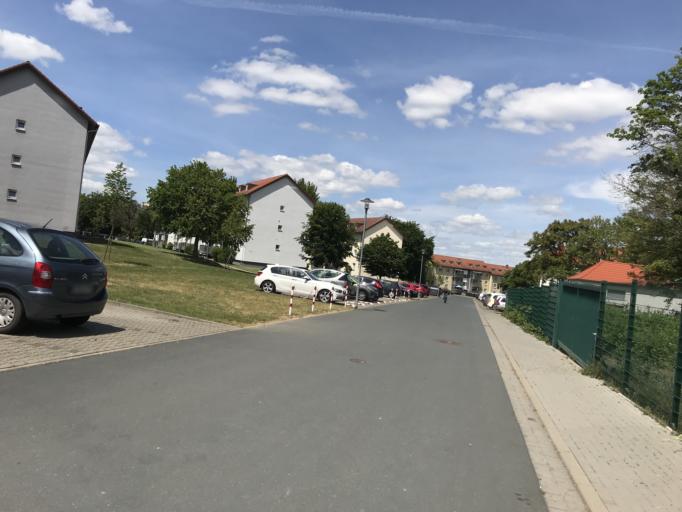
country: DE
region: Hesse
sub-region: Regierungsbezirk Darmstadt
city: Butzbach
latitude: 50.4394
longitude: 8.6606
